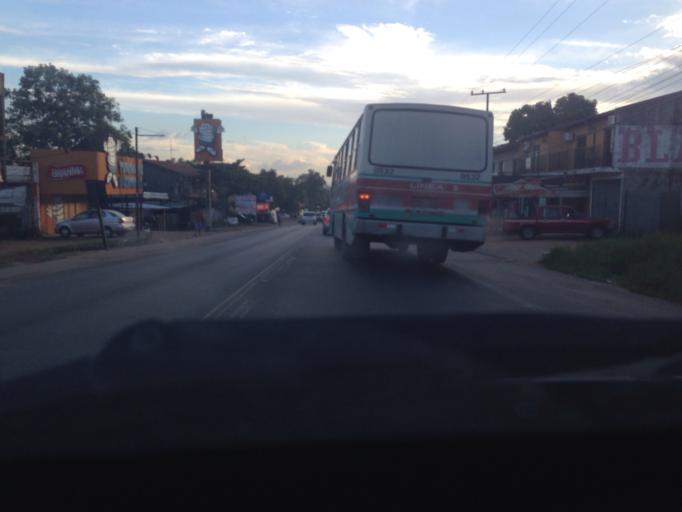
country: PY
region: Central
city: Lambare
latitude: -25.3504
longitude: -57.5914
